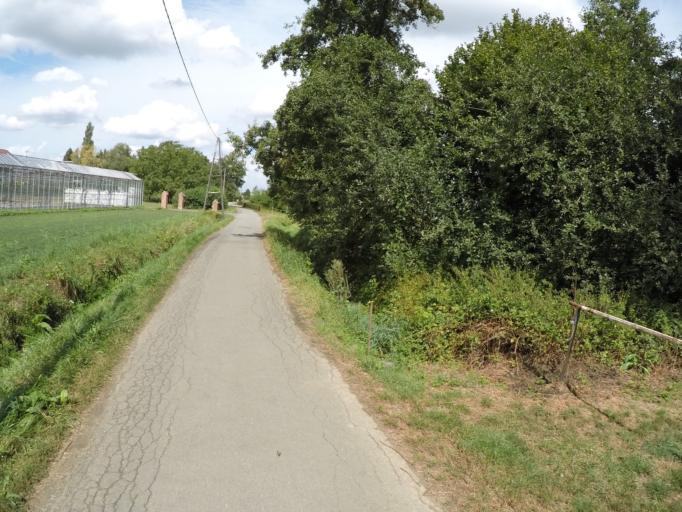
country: BE
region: Flanders
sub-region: Provincie Antwerpen
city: Wommelgem
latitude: 51.1859
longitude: 4.5331
